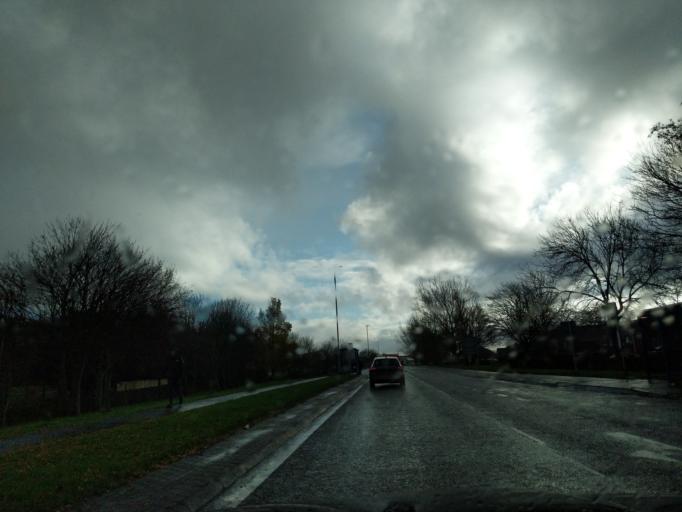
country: GB
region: England
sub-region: Northumberland
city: Blyth
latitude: 55.1183
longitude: -1.5108
